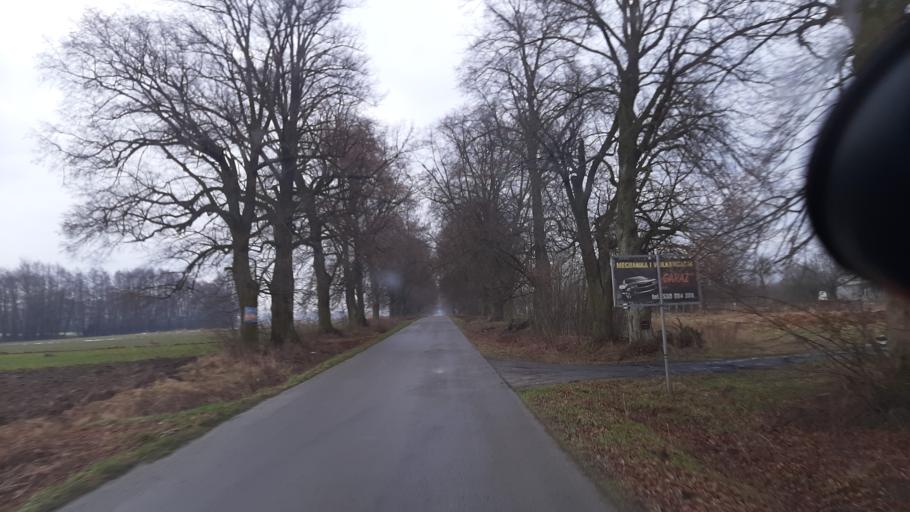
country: PL
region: Lublin Voivodeship
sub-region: Powiat lubelski
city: Jastkow
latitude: 51.3458
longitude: 22.5235
